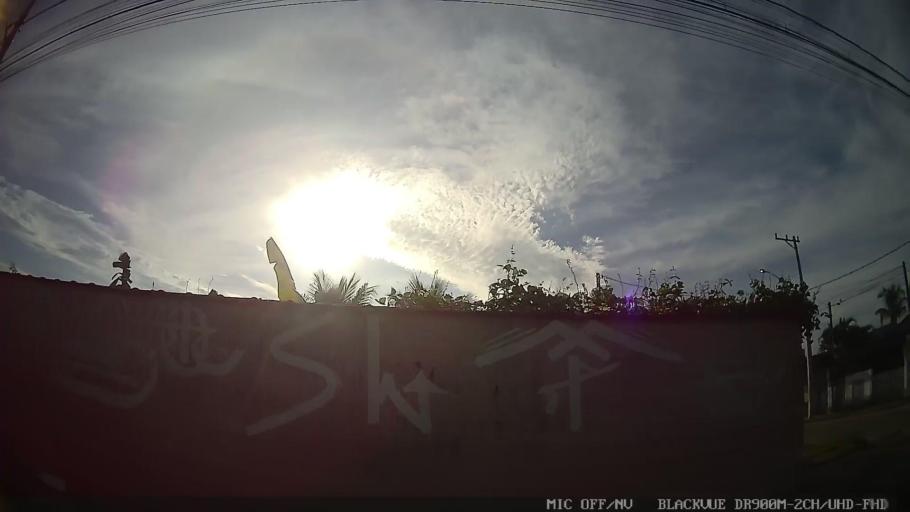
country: BR
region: Sao Paulo
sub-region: Itanhaem
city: Itanhaem
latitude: -24.1596
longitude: -46.7682
